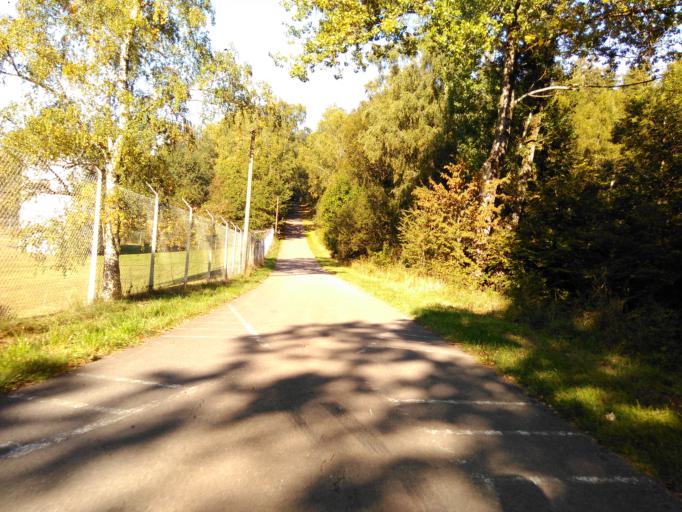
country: LU
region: Luxembourg
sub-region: Canton de Capellen
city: Steinfort
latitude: 49.6676
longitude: 5.9131
